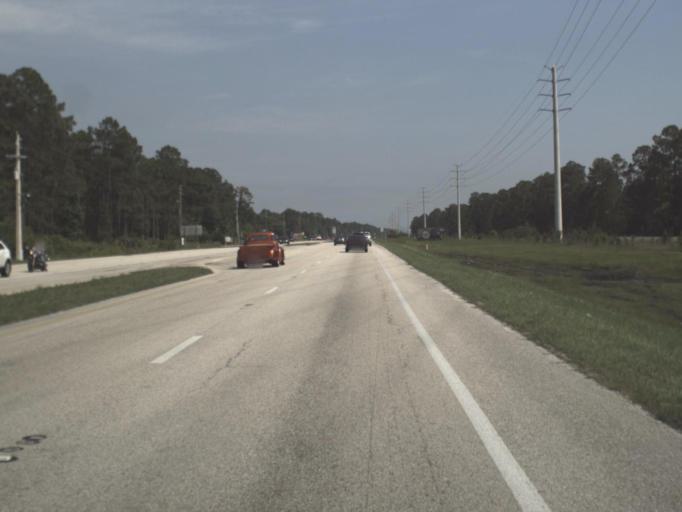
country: US
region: Florida
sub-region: Saint Johns County
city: Palm Valley
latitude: 30.0756
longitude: -81.4496
